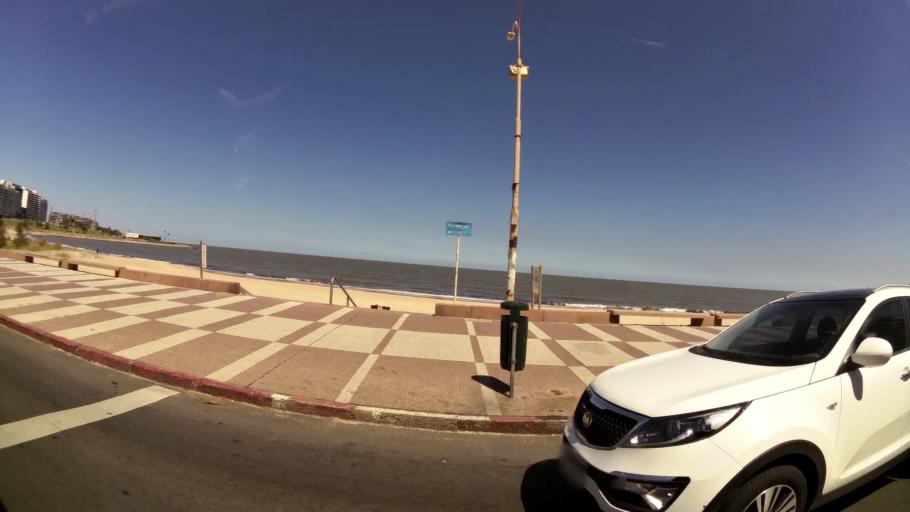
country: UY
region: Montevideo
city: Montevideo
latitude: -34.9111
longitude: -56.1448
